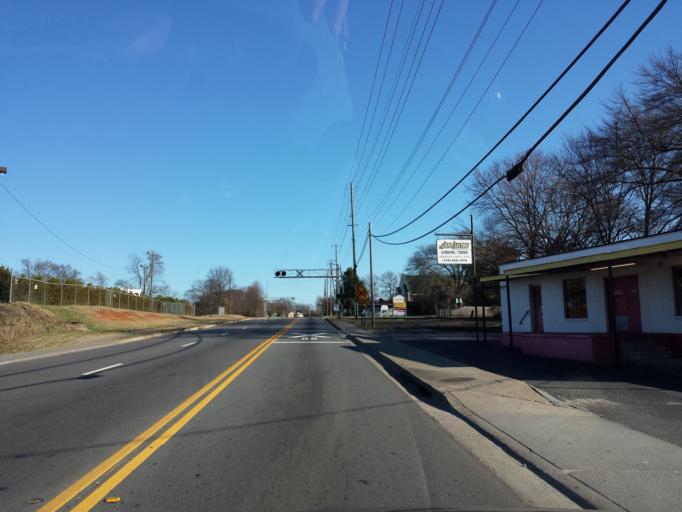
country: US
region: Georgia
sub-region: Cobb County
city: Marietta
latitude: 33.9767
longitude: -84.5547
